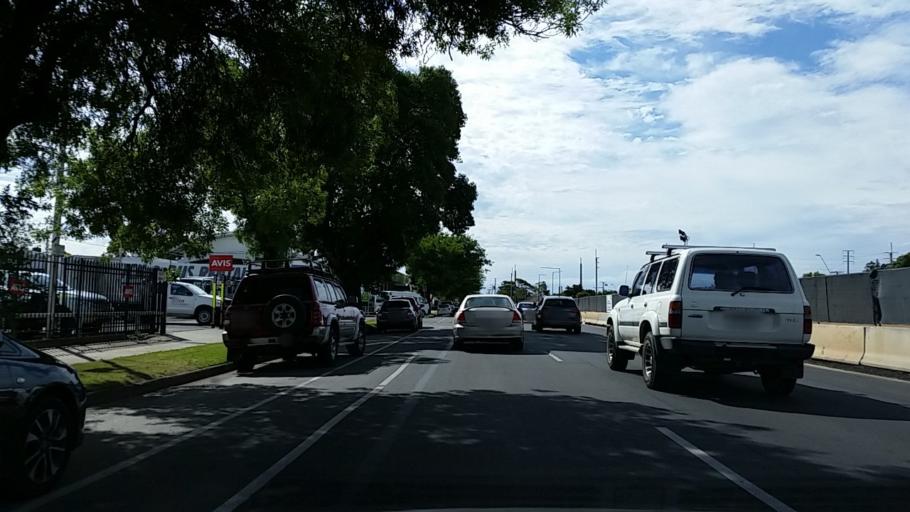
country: AU
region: South Australia
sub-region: Charles Sturt
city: Allenby Gardens
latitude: -34.9008
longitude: 138.5648
